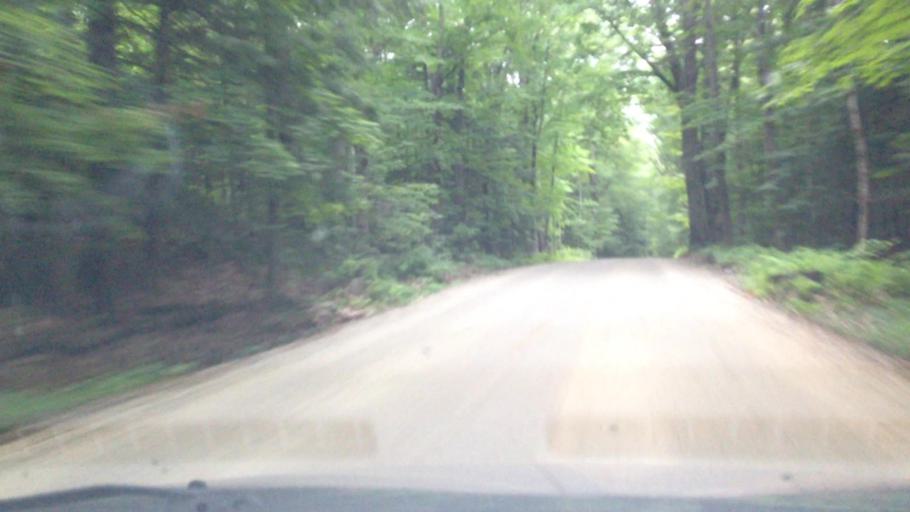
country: US
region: New Hampshire
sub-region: Cheshire County
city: Marlborough
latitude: 42.8952
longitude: -72.1742
